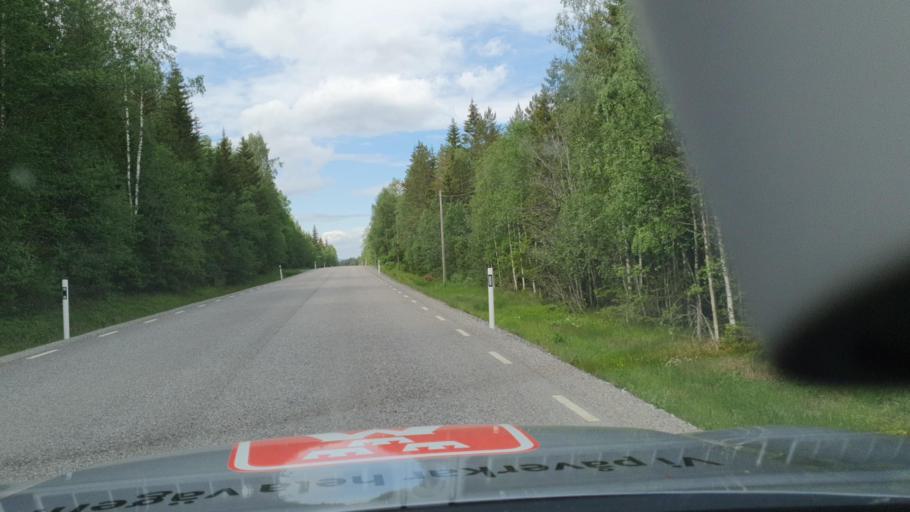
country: SE
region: Vaesternorrland
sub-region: Kramfors Kommun
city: Kramfors
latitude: 62.9194
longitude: 17.9515
